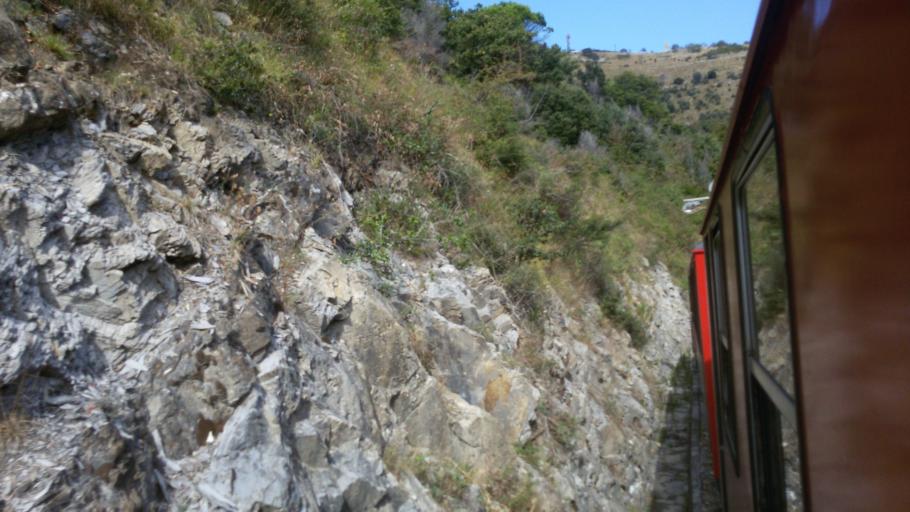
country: IT
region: Liguria
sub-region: Provincia di Genova
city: Genoa
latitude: 44.4374
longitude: 8.9385
